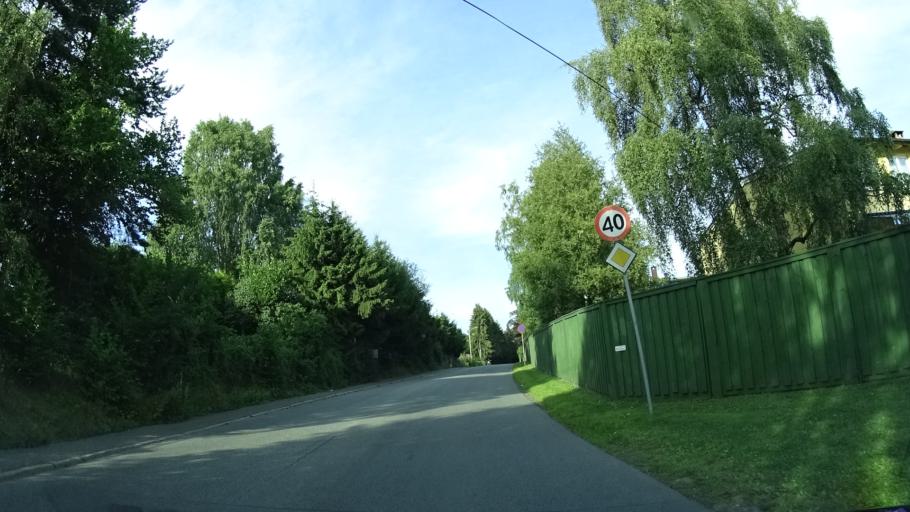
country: NO
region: Oslo
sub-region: Oslo
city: Sjolyststranda
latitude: 59.9506
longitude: 10.6667
